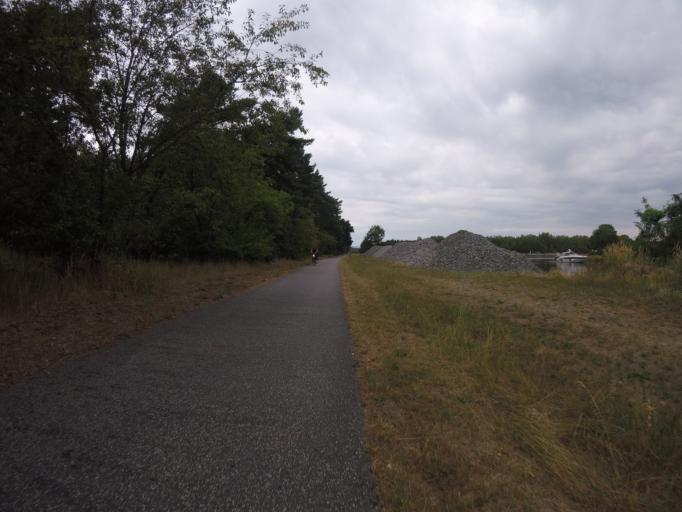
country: DE
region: Brandenburg
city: Oranienburg
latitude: 52.7746
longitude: 13.2794
